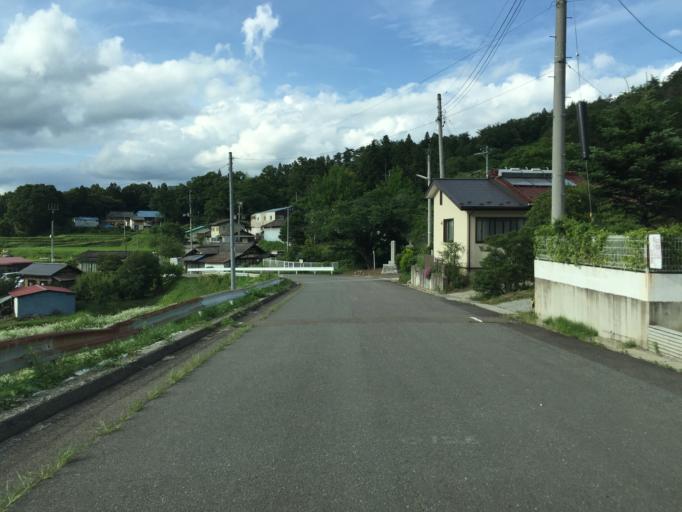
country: JP
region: Fukushima
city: Fukushima-shi
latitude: 37.6896
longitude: 140.5260
